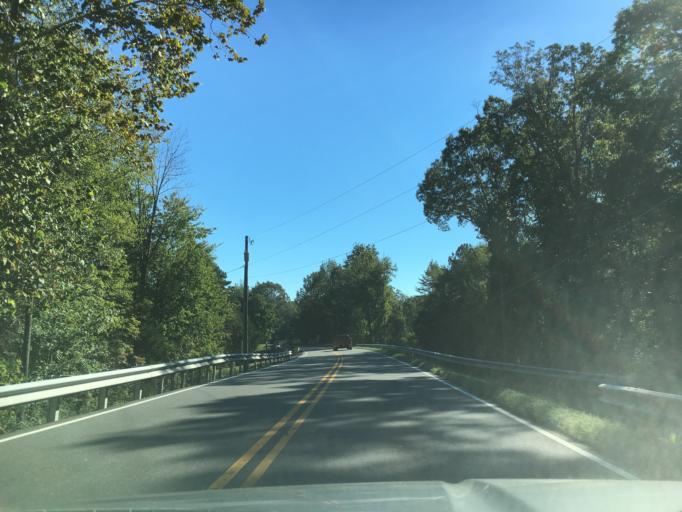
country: US
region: Virginia
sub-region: Goochland County
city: Goochland
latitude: 37.6986
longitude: -77.8574
